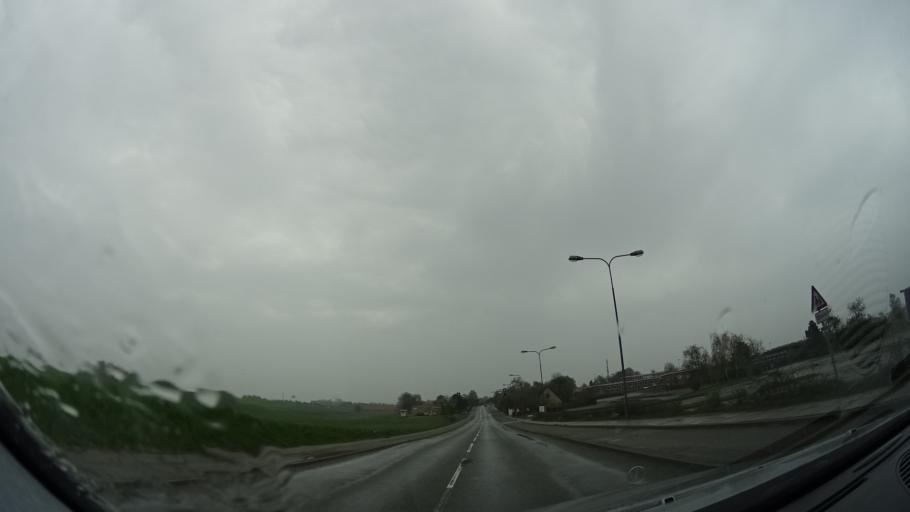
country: DK
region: Zealand
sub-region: Odsherred Kommune
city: Hojby
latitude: 55.8538
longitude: 11.5704
